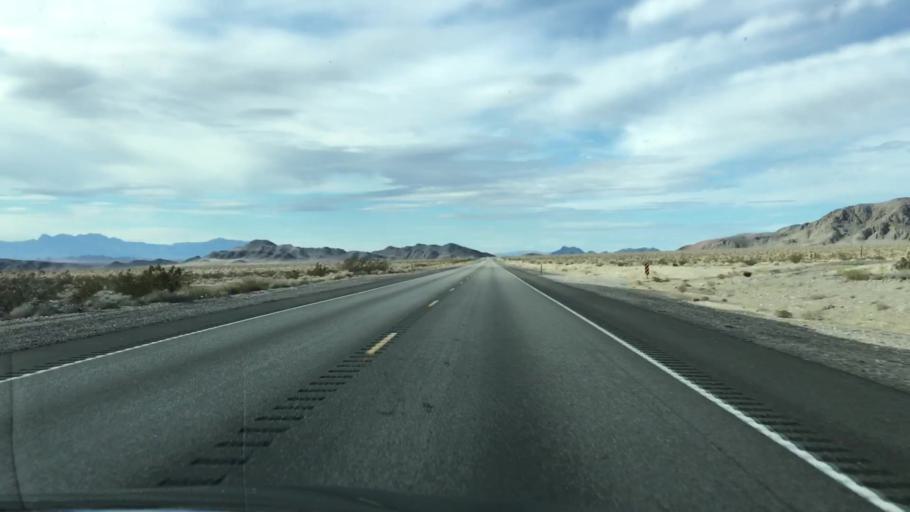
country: US
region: Nevada
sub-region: Nye County
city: Pahrump
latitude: 36.5706
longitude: -116.1642
